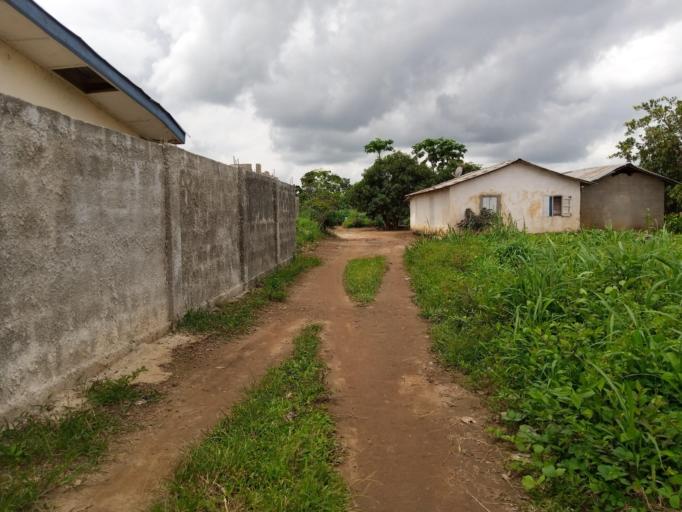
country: SL
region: Southern Province
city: Moyamba
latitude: 8.1630
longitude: -12.4235
